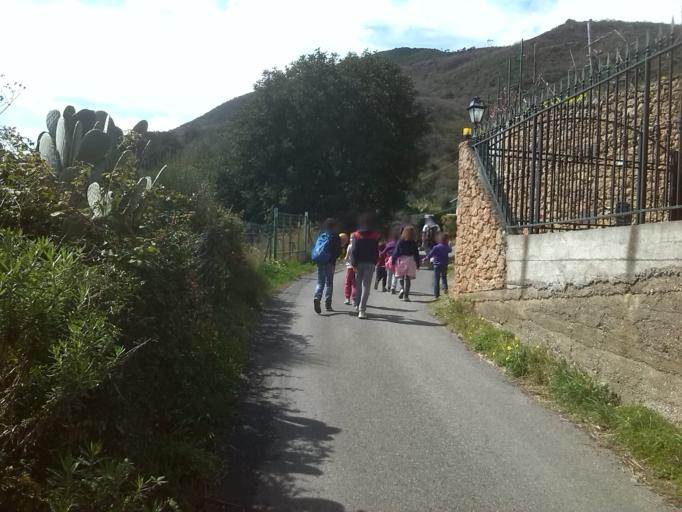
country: IT
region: Liguria
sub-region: Provincia di Savona
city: Albenga
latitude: 44.0350
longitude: 8.2025
